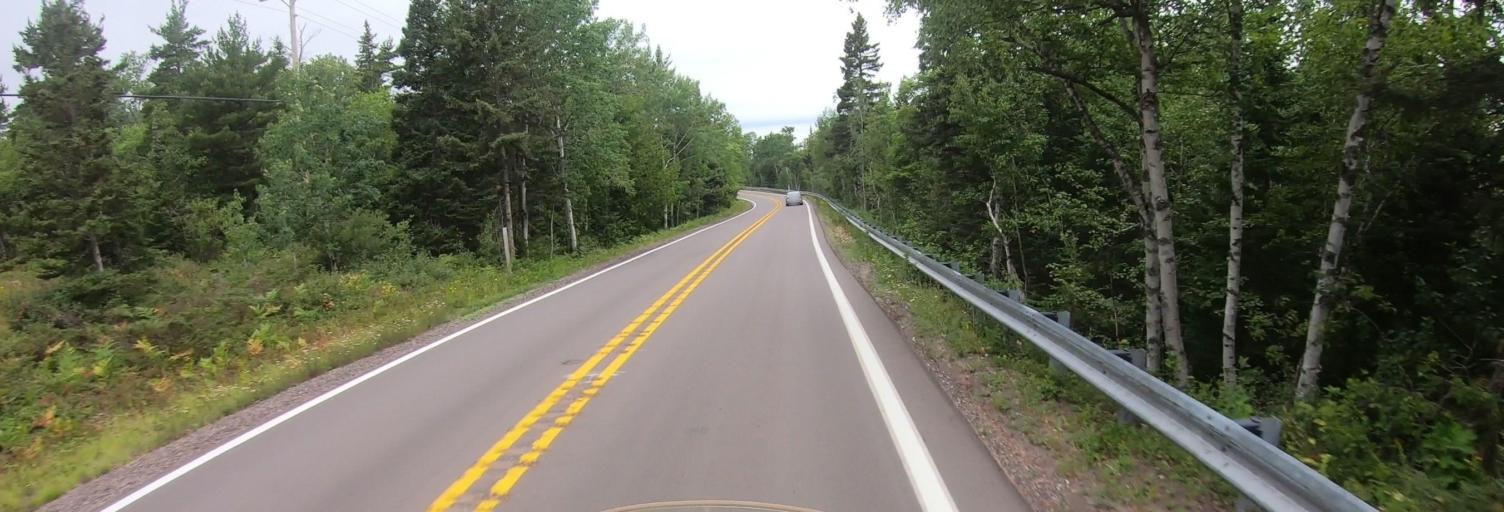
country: US
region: Michigan
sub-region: Keweenaw County
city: Eagle River
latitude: 47.4777
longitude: -87.9893
